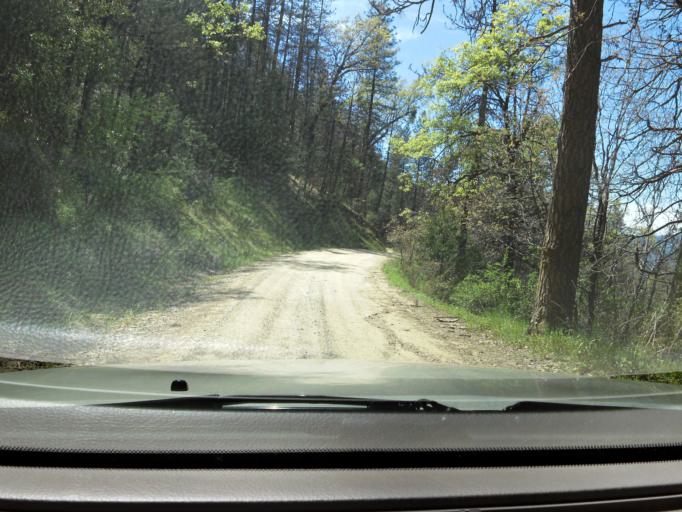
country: US
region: California
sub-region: Madera County
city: Oakhurst
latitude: 37.2837
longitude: -119.5873
